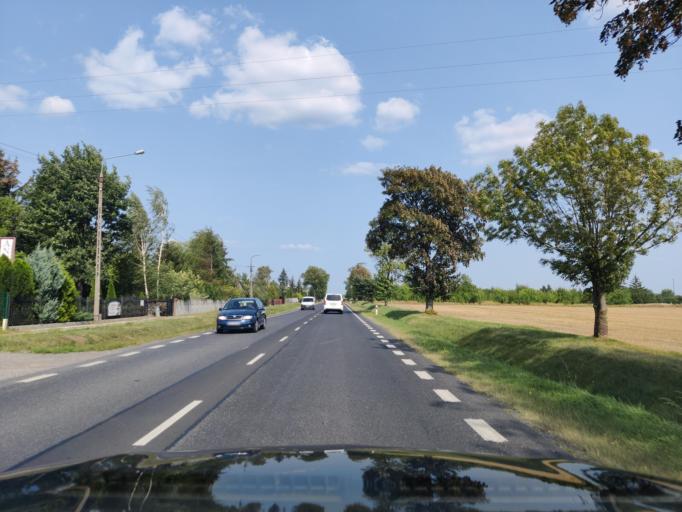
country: PL
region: Masovian Voivodeship
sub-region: Powiat makowski
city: Rozan
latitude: 52.8847
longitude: 21.3836
